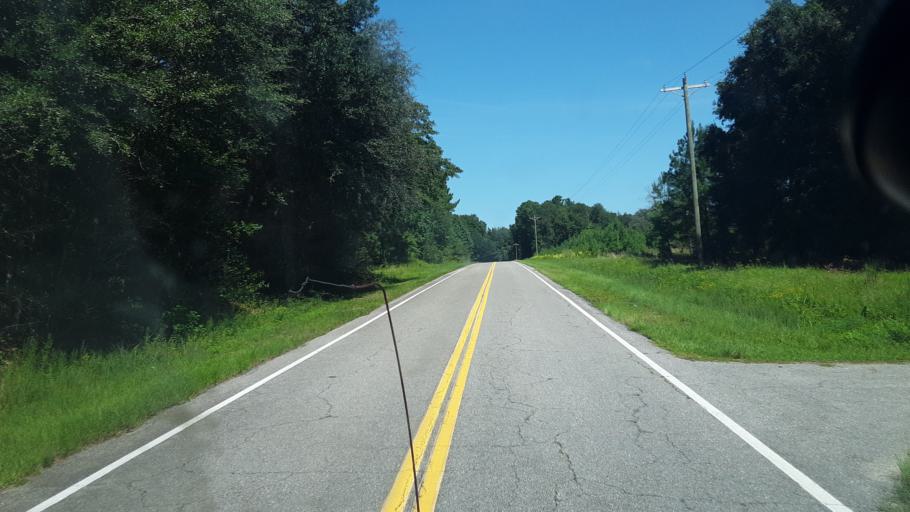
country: US
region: South Carolina
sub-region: Hampton County
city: Varnville
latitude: 32.9579
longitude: -81.0413
